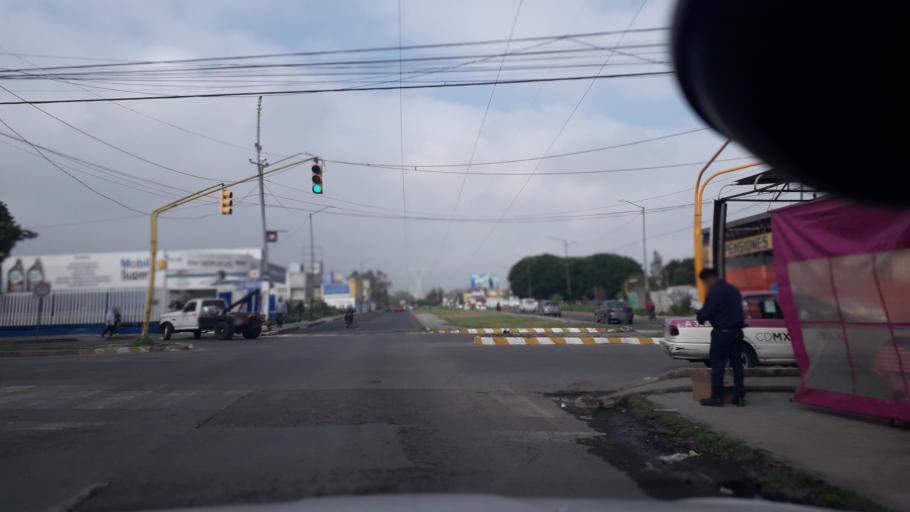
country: MX
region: Mexico
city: Coacalco
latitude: 19.6444
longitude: -99.0868
